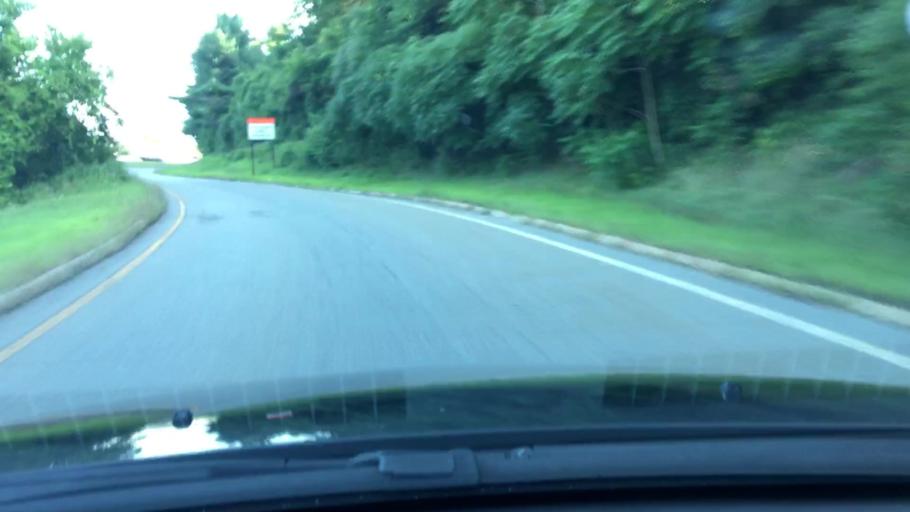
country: US
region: Massachusetts
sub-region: Worcester County
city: West Boylston
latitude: 42.3357
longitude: -71.7992
